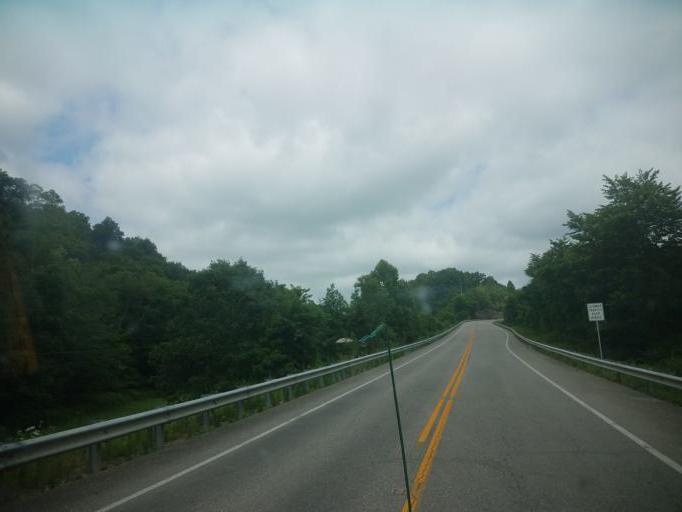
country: US
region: Kentucky
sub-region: Metcalfe County
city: Edmonton
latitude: 36.8482
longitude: -85.6373
